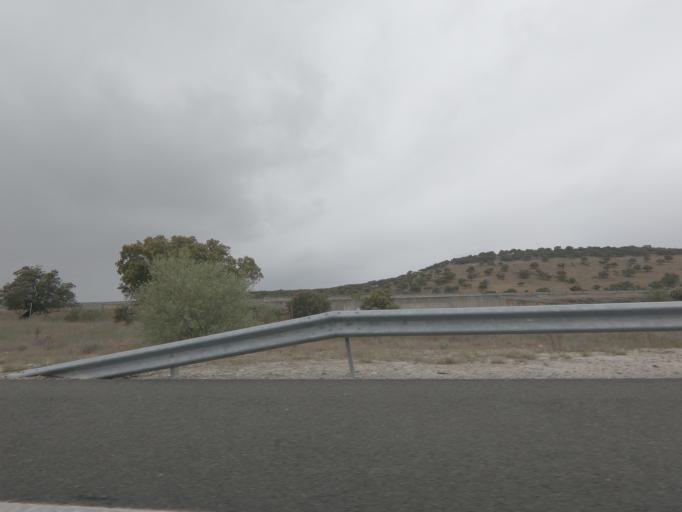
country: ES
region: Extremadura
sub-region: Provincia de Caceres
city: Villar de Plasencia
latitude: 40.1577
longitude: -6.0310
